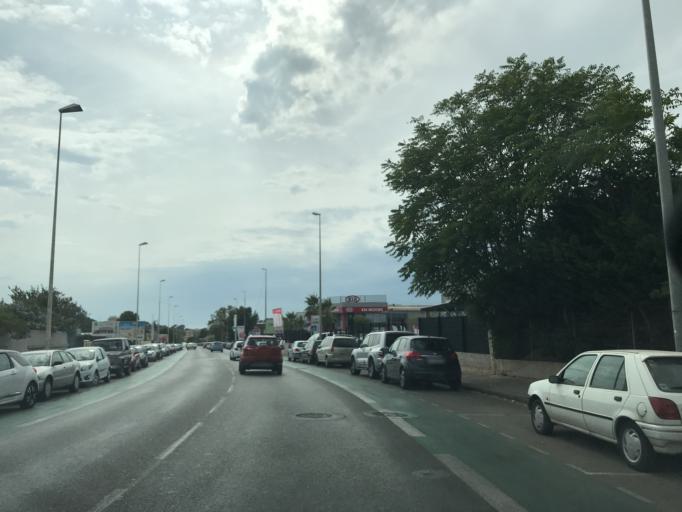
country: FR
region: Provence-Alpes-Cote d'Azur
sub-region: Departement du Var
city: La Valette-du-Var
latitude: 43.1285
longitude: 5.9794
